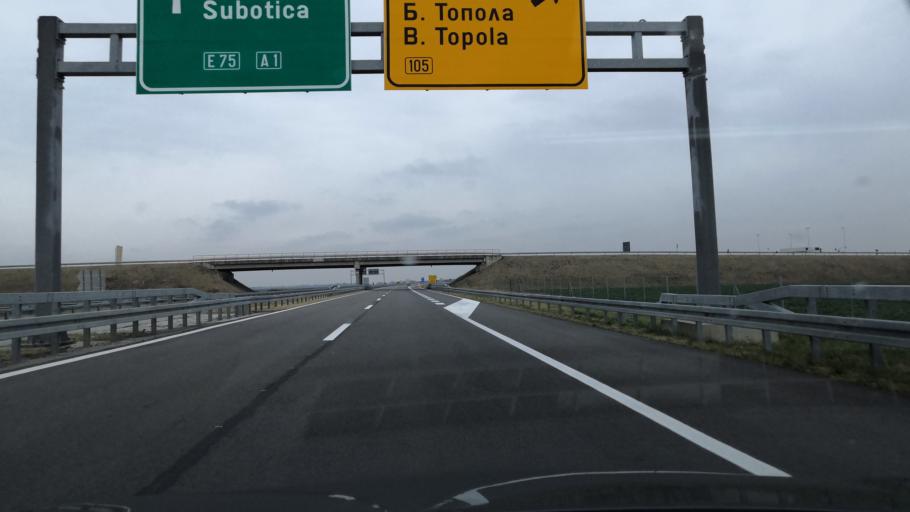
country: RS
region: Autonomna Pokrajina Vojvodina
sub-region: Severnobacki Okrug
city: Backa Topola
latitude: 45.8227
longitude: 19.6871
